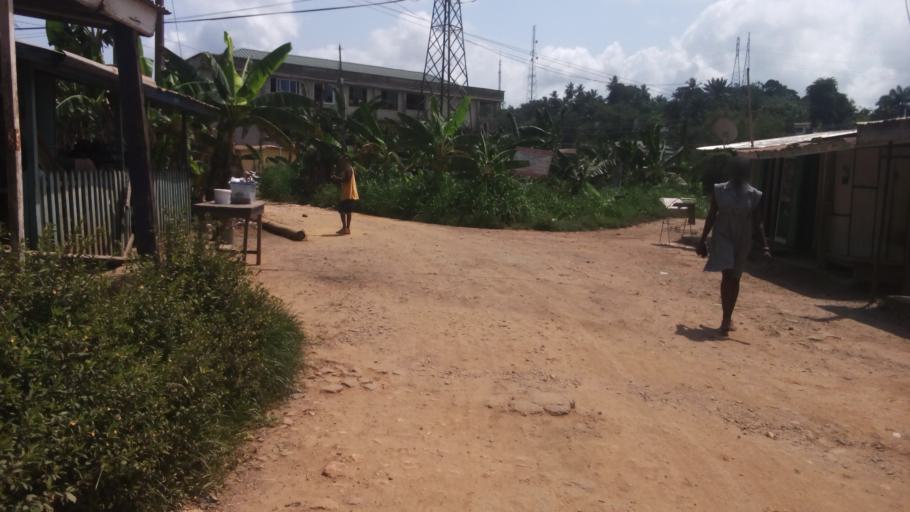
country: GH
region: Western
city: Tarkwa
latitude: 5.3009
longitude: -1.9985
